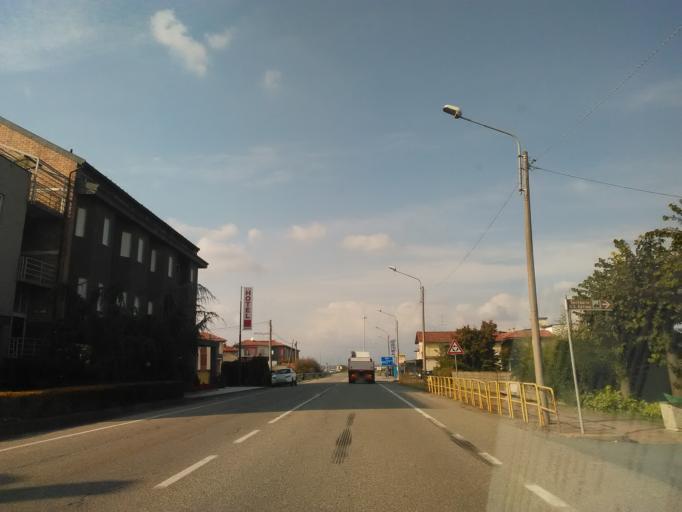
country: IT
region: Piedmont
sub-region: Provincia di Vercelli
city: Buronzo
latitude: 45.4448
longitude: 8.2334
